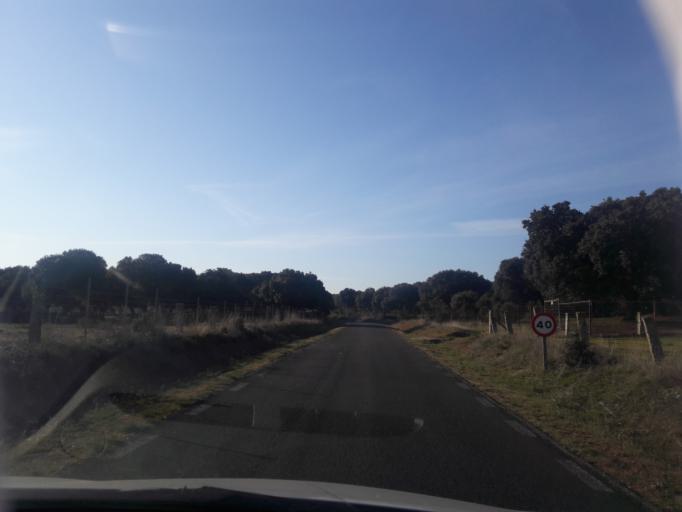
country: ES
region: Castille and Leon
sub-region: Provincia de Salamanca
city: Montejo
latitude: 40.6224
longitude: -5.6098
